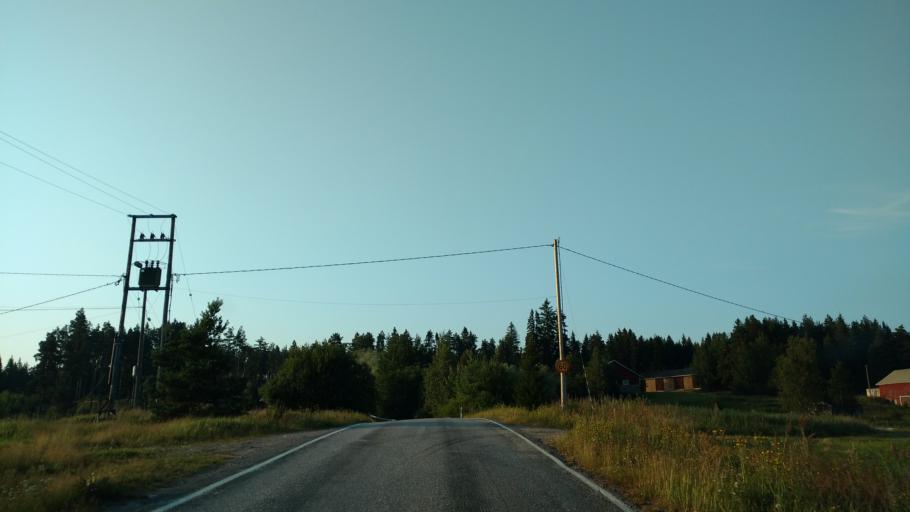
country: FI
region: Varsinais-Suomi
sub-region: Salo
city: Saerkisalo
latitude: 60.1783
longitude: 22.9661
